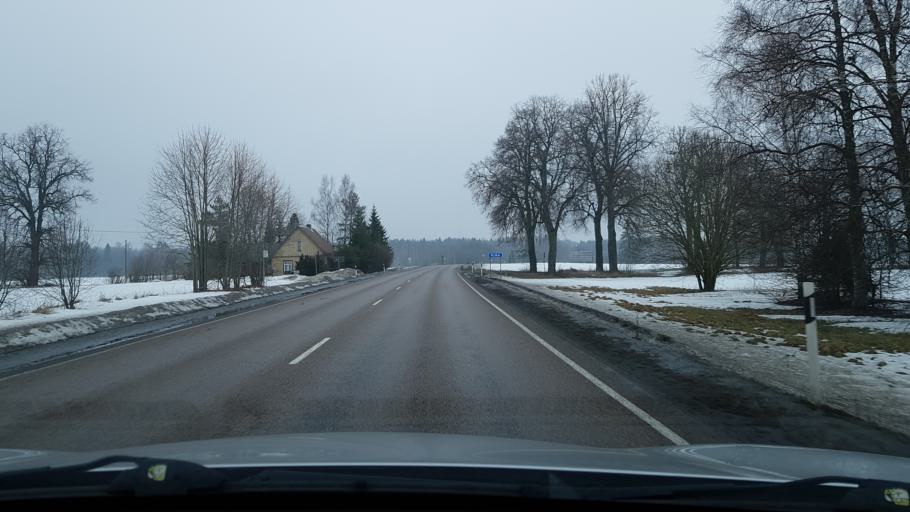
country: EE
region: Valgamaa
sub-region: Torva linn
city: Torva
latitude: 58.0510
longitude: 26.1929
